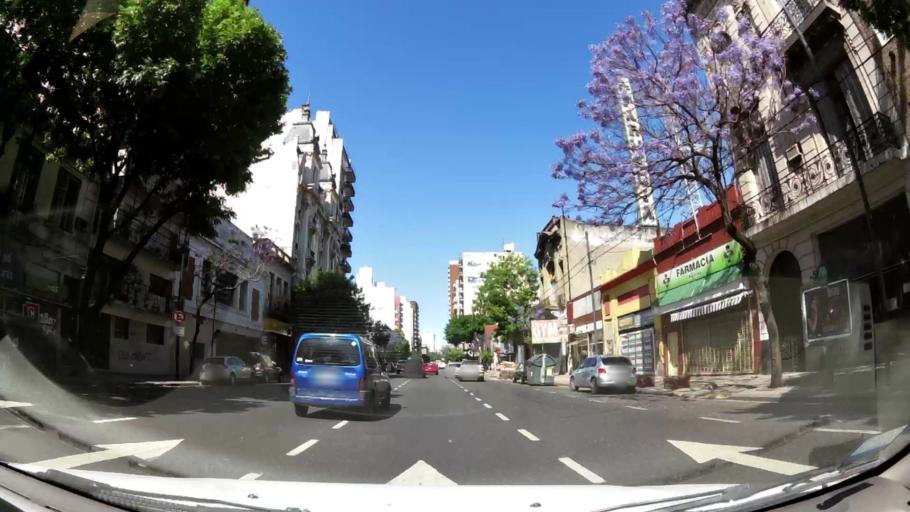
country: AR
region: Buenos Aires F.D.
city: Buenos Aires
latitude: -34.6234
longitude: -58.3990
